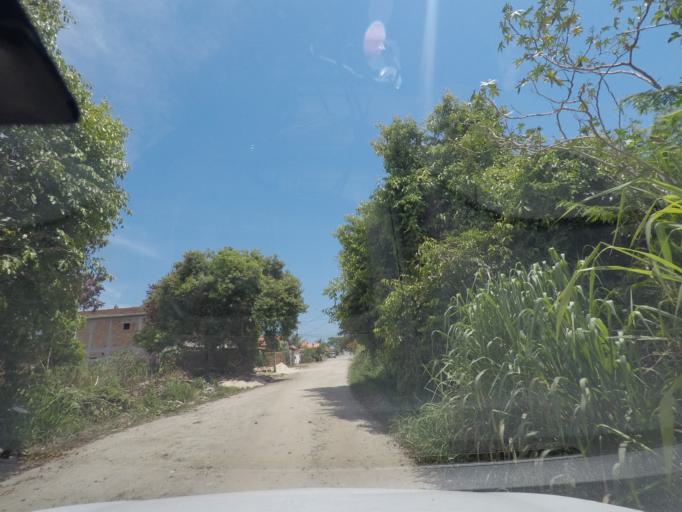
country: BR
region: Rio de Janeiro
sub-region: Niteroi
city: Niteroi
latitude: -22.9588
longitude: -42.9694
